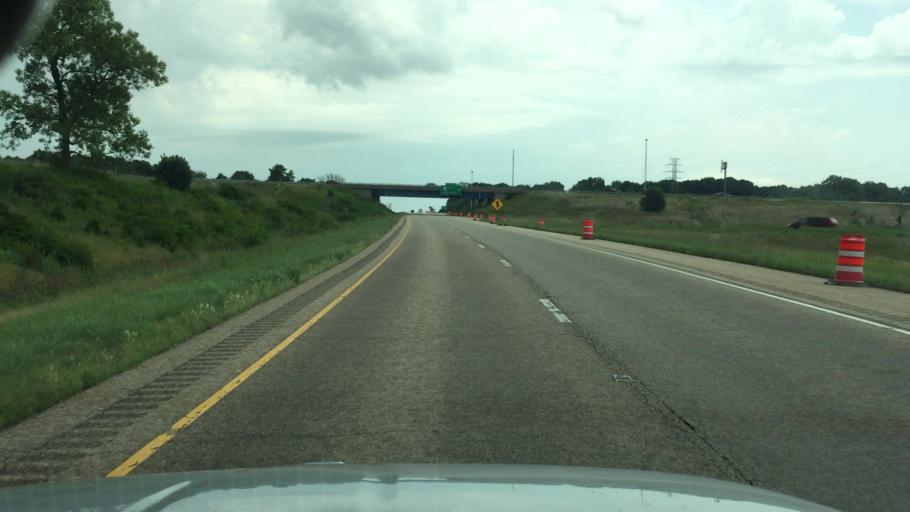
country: US
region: Illinois
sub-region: Peoria County
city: Bellevue
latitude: 40.7419
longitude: -89.6708
